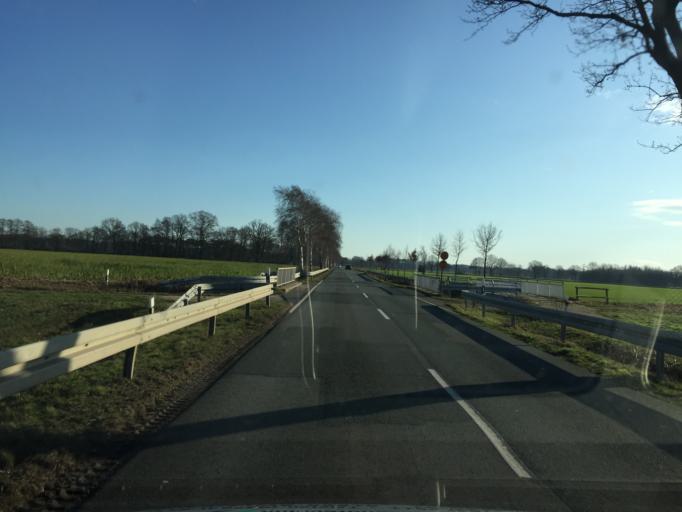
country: DE
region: Lower Saxony
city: Estorf
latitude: 52.5552
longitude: 9.1833
